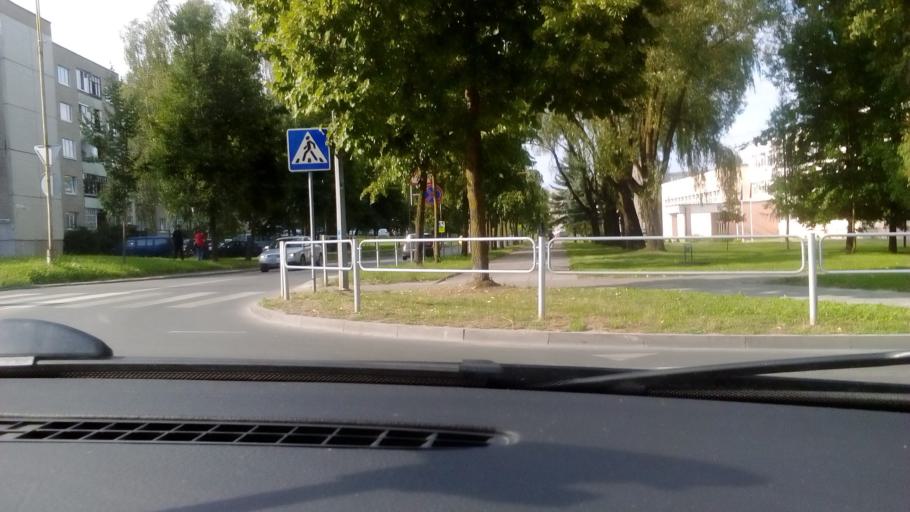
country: LT
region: Alytaus apskritis
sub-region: Alytus
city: Alytus
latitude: 54.3943
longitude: 24.0212
